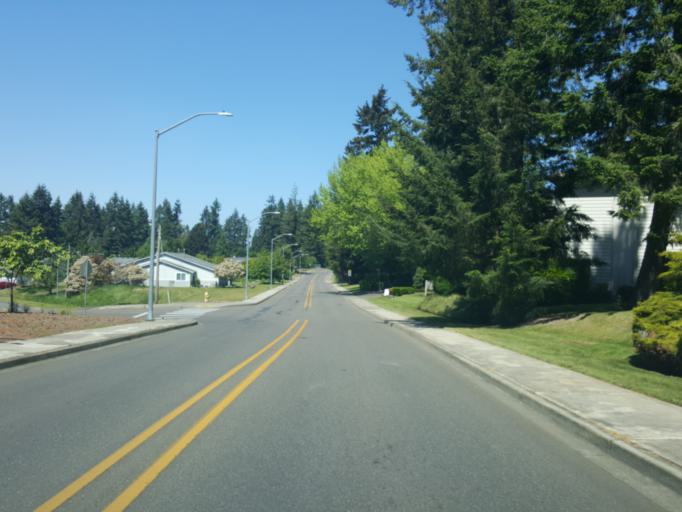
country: US
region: Washington
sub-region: Pierce County
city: Steilacoom
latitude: 47.1624
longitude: -122.5877
